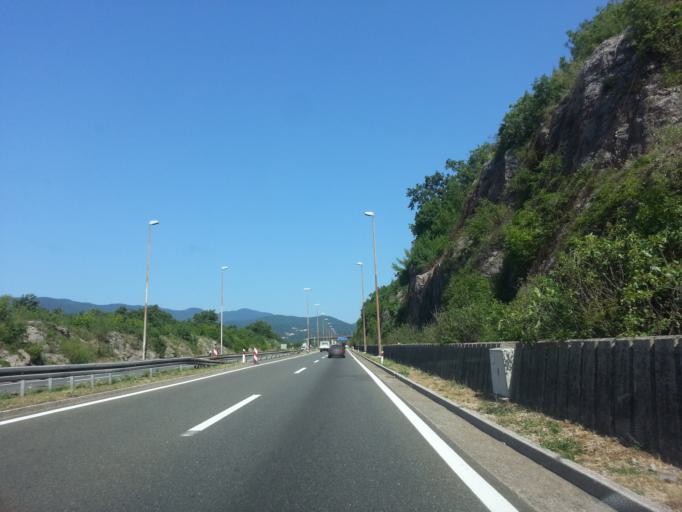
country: HR
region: Primorsko-Goranska
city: Rubesi
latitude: 45.3576
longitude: 14.3448
